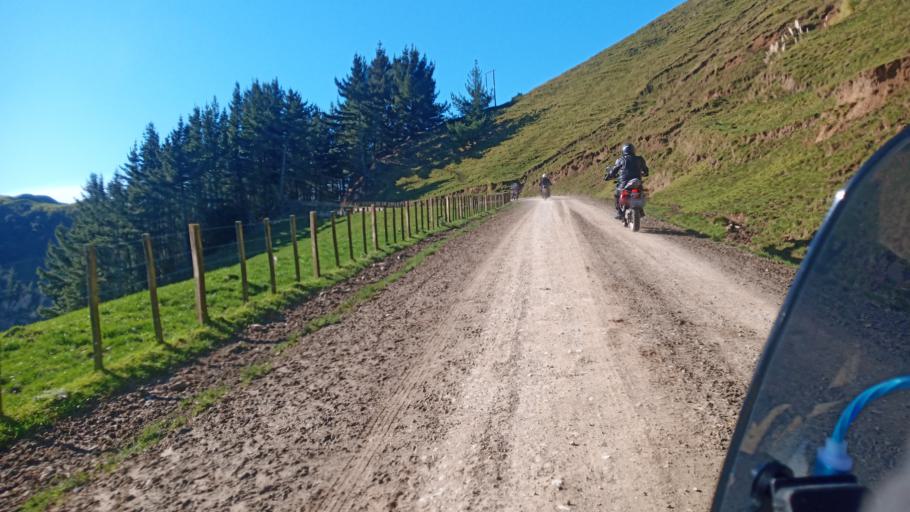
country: NZ
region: Gisborne
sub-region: Gisborne District
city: Gisborne
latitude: -38.2872
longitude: 177.8571
